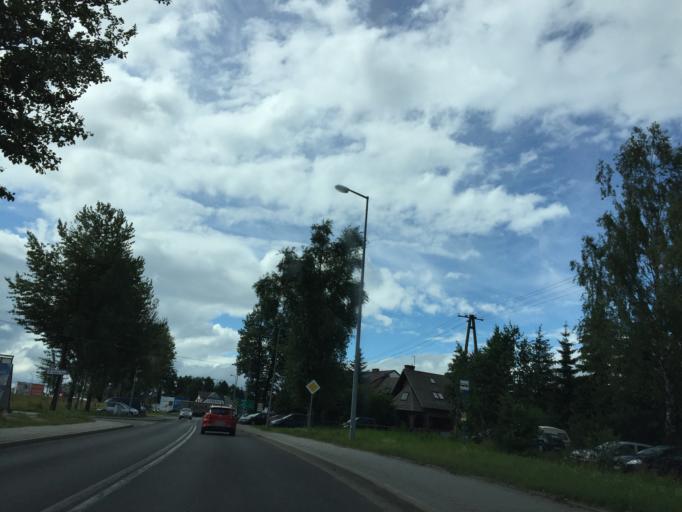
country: PL
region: Lesser Poland Voivodeship
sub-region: Powiat nowotarski
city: Nowy Targ
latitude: 49.4754
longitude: 20.0528
